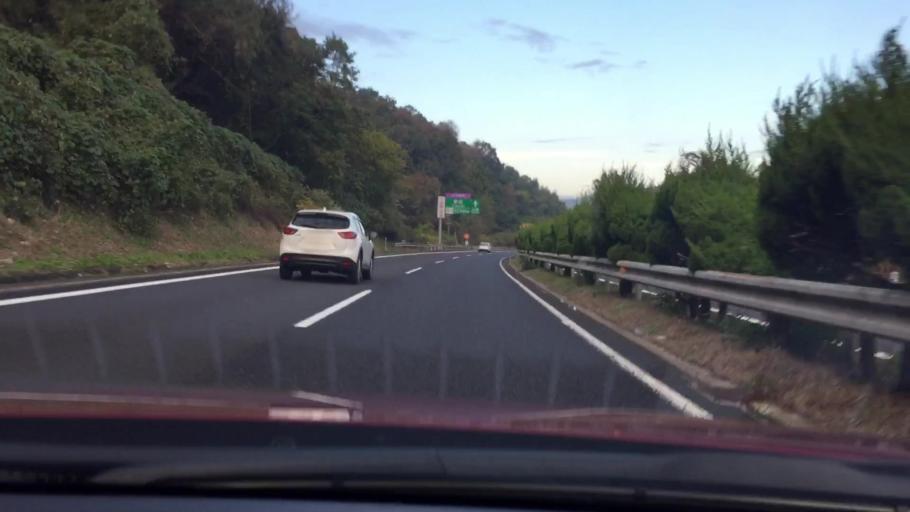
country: JP
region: Hyogo
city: Himeji
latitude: 34.9607
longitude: 134.7002
